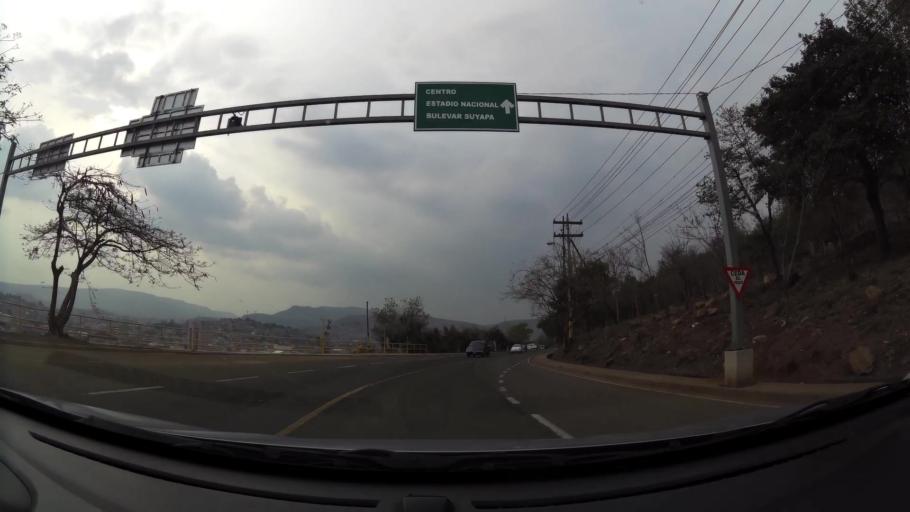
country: HN
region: Francisco Morazan
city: Tegucigalpa
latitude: 14.0911
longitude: -87.2033
